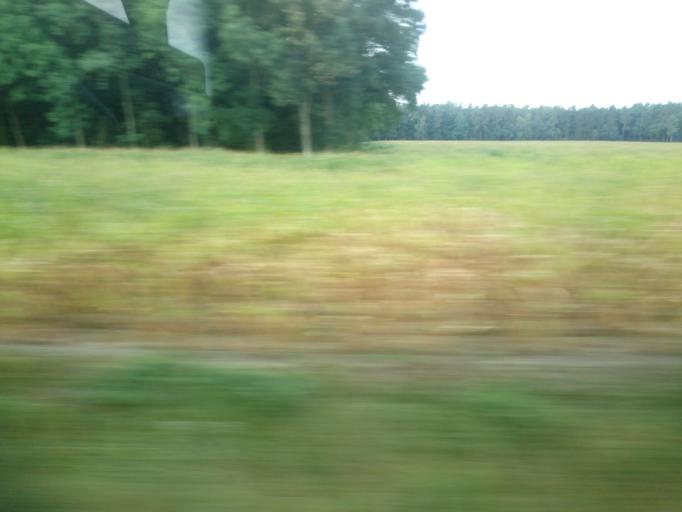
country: DE
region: Mecklenburg-Vorpommern
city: Ducherow
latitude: 53.7225
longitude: 13.8208
